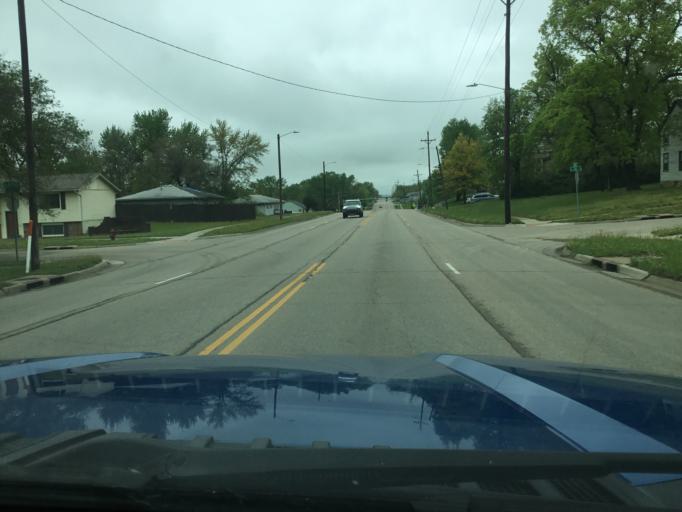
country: US
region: Kansas
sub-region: Shawnee County
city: Topeka
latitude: 39.0204
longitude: -95.6701
